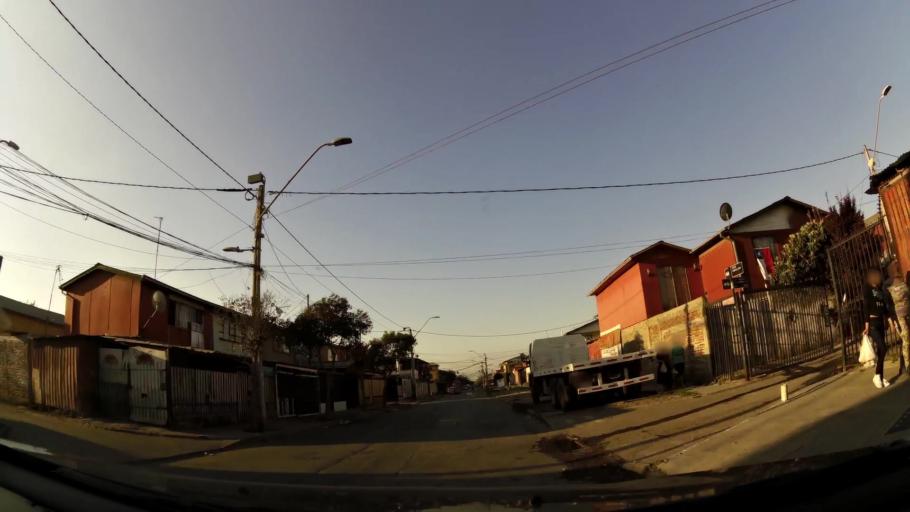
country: CL
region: Santiago Metropolitan
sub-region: Provincia de Maipo
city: San Bernardo
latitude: -33.6006
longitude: -70.6729
